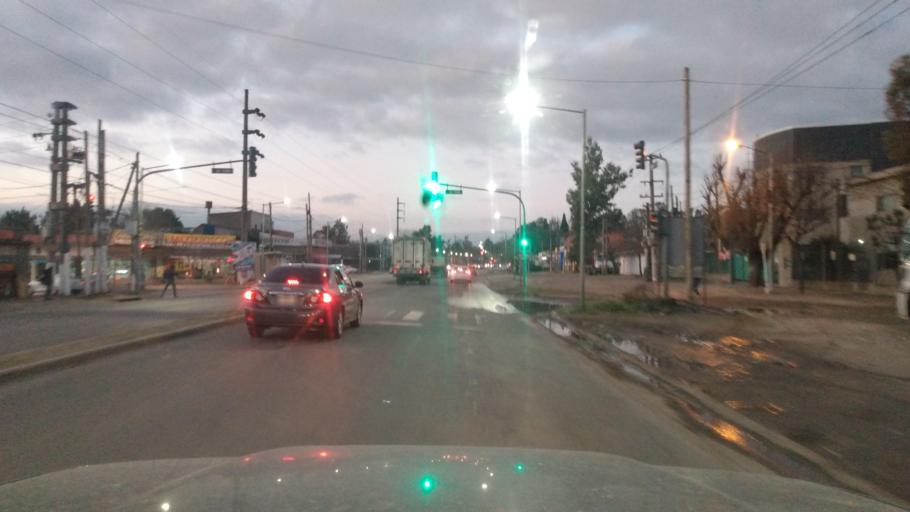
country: AR
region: Buenos Aires
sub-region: Partido de Pilar
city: Pilar
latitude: -34.4459
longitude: -58.9028
